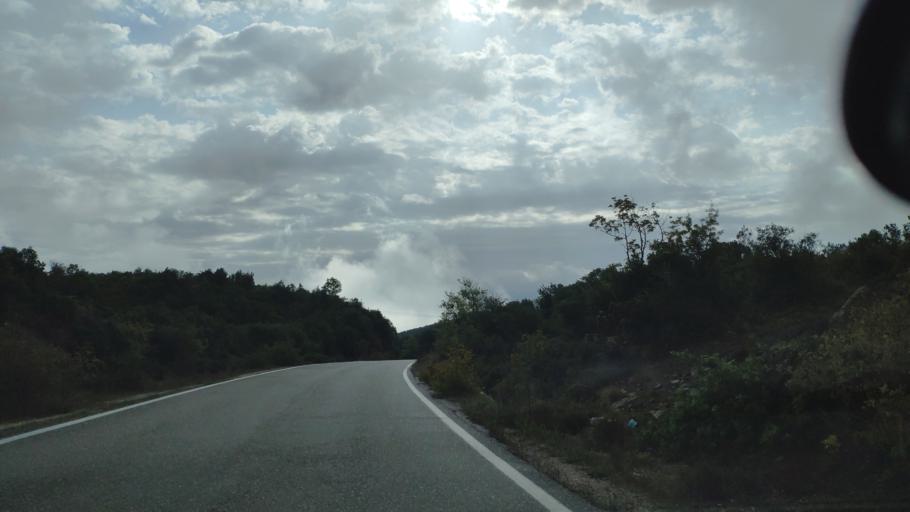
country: GR
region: West Greece
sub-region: Nomos Aitolias kai Akarnanias
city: Sardinia
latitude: 38.8766
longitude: 21.2681
